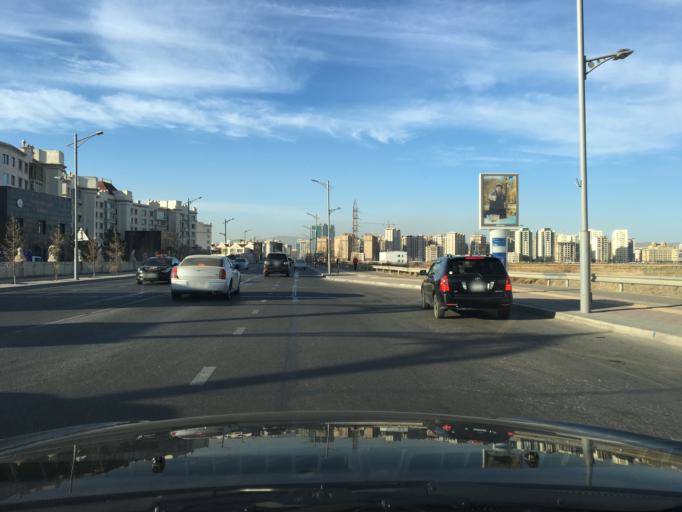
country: MN
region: Ulaanbaatar
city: Ulaanbaatar
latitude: 47.8926
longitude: 106.9370
